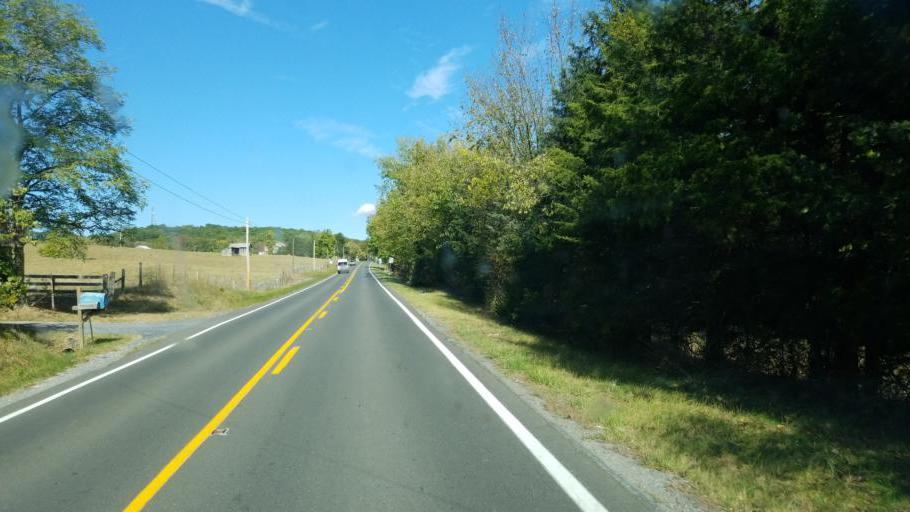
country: US
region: Virginia
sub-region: Warren County
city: Front Royal
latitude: 38.8260
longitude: -78.3263
